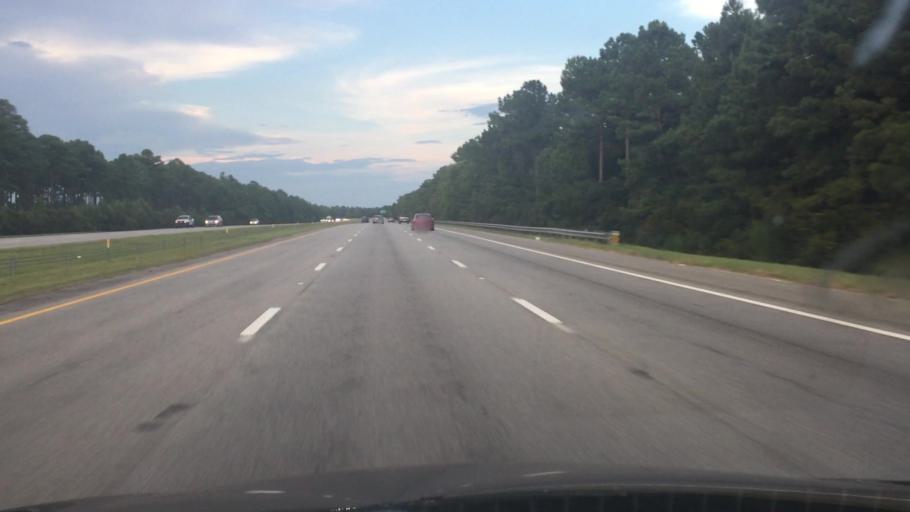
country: US
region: South Carolina
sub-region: Horry County
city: Myrtle Beach
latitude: 33.7760
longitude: -78.8148
